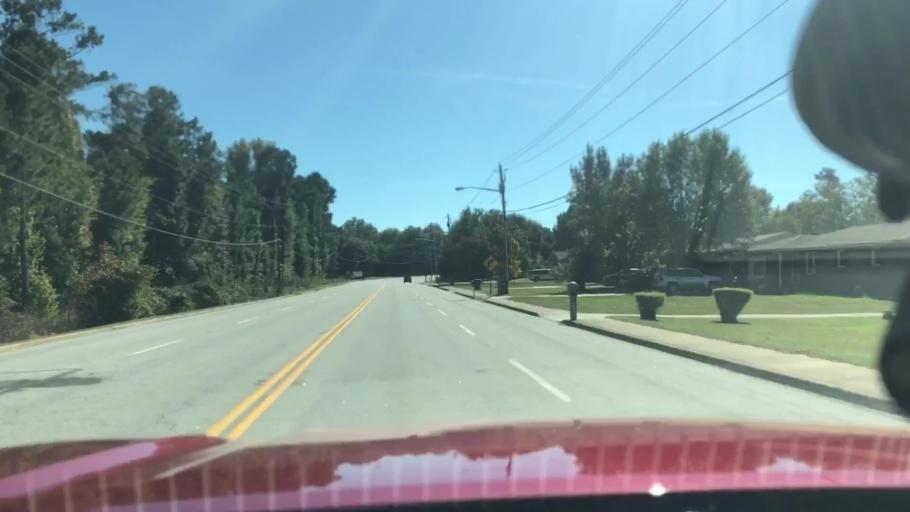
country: US
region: South Carolina
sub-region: Greenwood County
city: Greenwood
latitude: 34.2216
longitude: -82.1401
